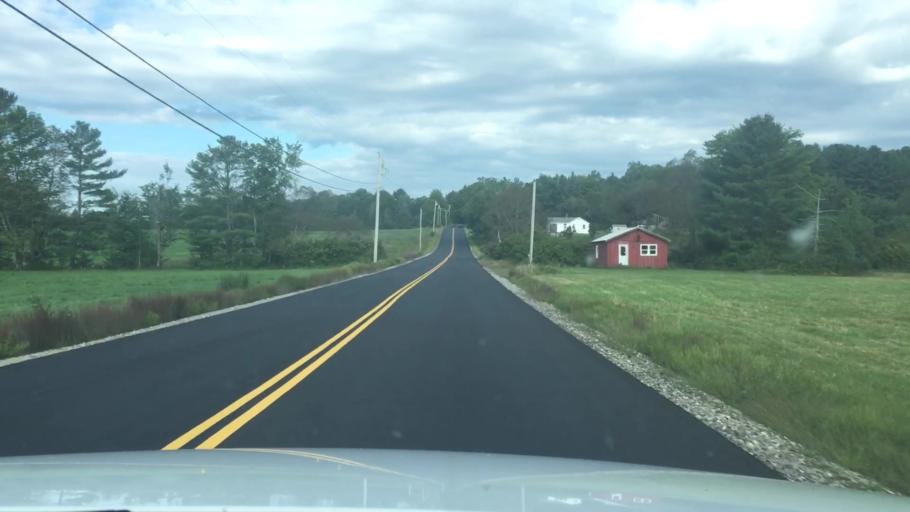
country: US
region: Maine
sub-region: Androscoggin County
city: Lisbon Falls
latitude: 44.0399
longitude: -70.0357
